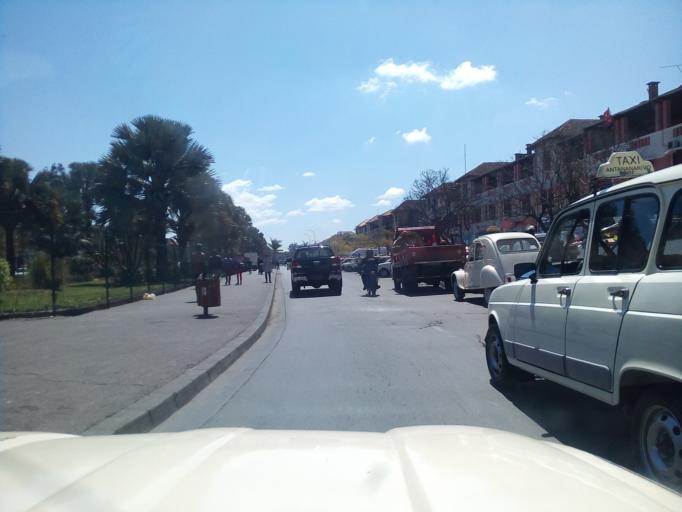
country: MG
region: Analamanga
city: Antananarivo
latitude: -18.9073
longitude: 47.5249
